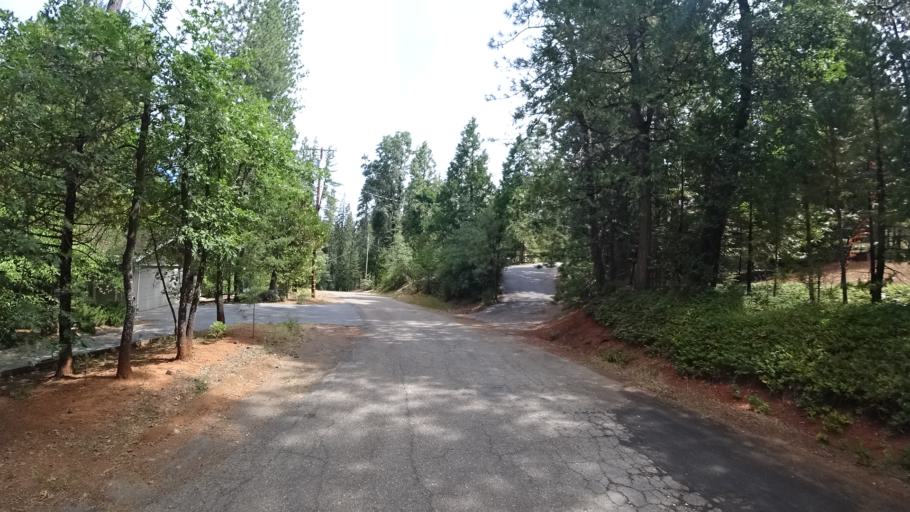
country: US
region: California
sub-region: Calaveras County
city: Arnold
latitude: 38.2406
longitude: -120.3569
